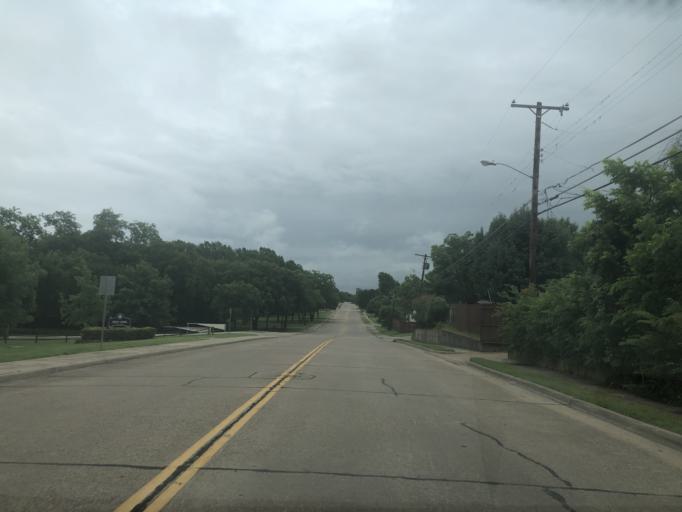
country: US
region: Texas
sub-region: Dallas County
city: Irving
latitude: 32.7939
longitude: -96.9399
